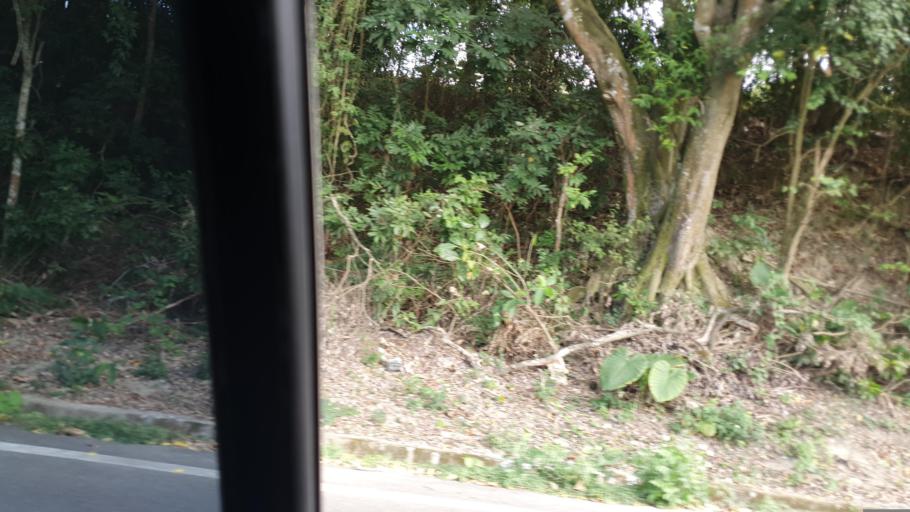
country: TW
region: Taiwan
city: Yujing
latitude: 23.0324
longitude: 120.4155
